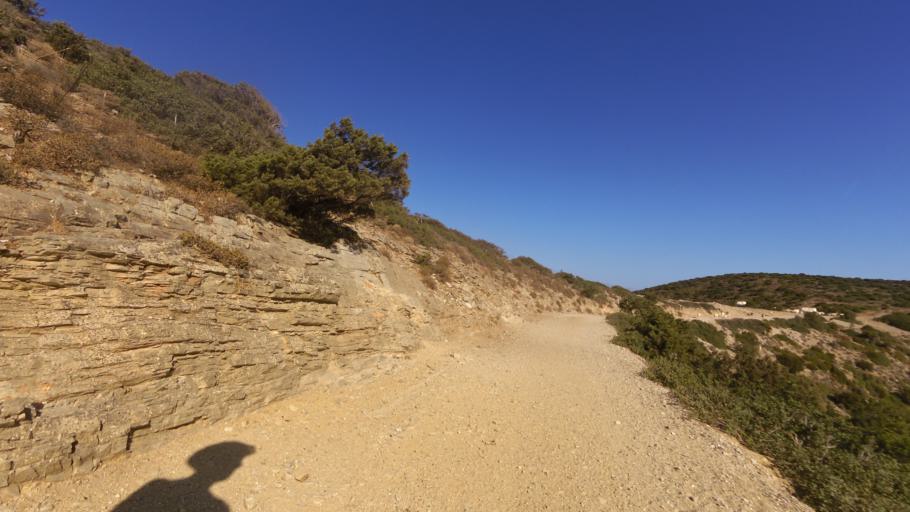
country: GR
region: South Aegean
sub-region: Nomos Kykladon
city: Antiparos
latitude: 36.9882
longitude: 25.0286
